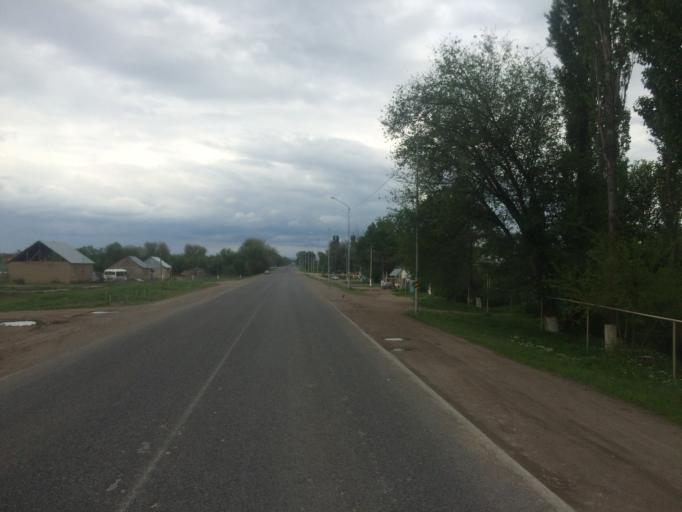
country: KZ
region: Zhambyl
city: Georgiyevka
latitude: 43.2270
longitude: 74.3980
